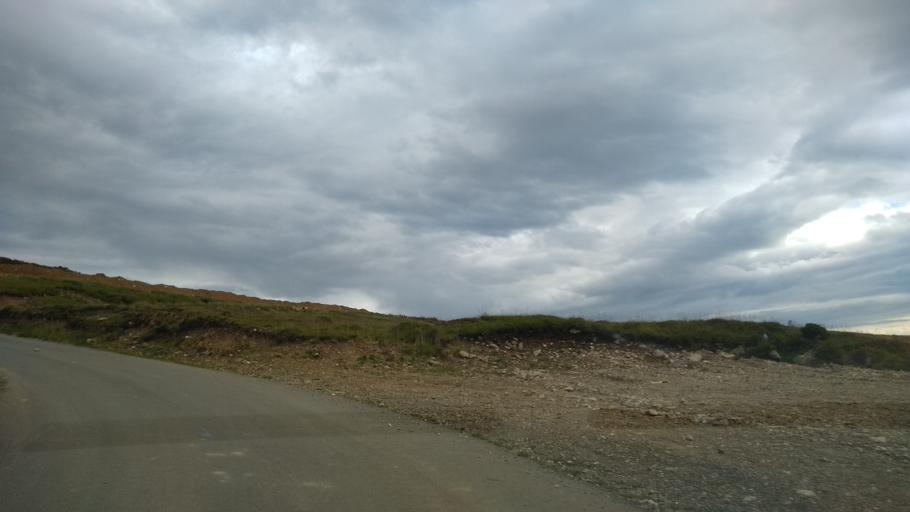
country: RO
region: Hunedoara
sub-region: Municipiul  Vulcan
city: Jiu-Paroseni
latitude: 45.3037
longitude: 23.3125
